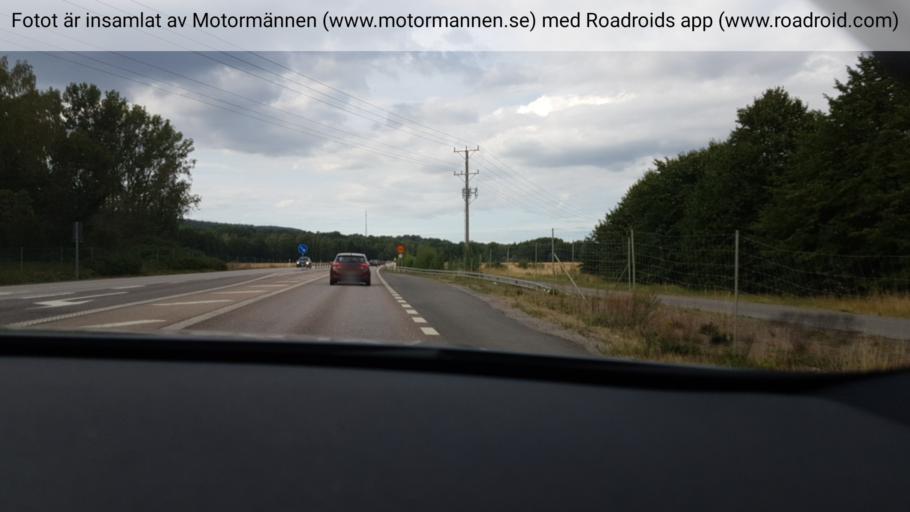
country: SE
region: Vaestra Goetaland
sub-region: Skovde Kommun
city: Stopen
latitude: 58.4433
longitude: 13.8535
